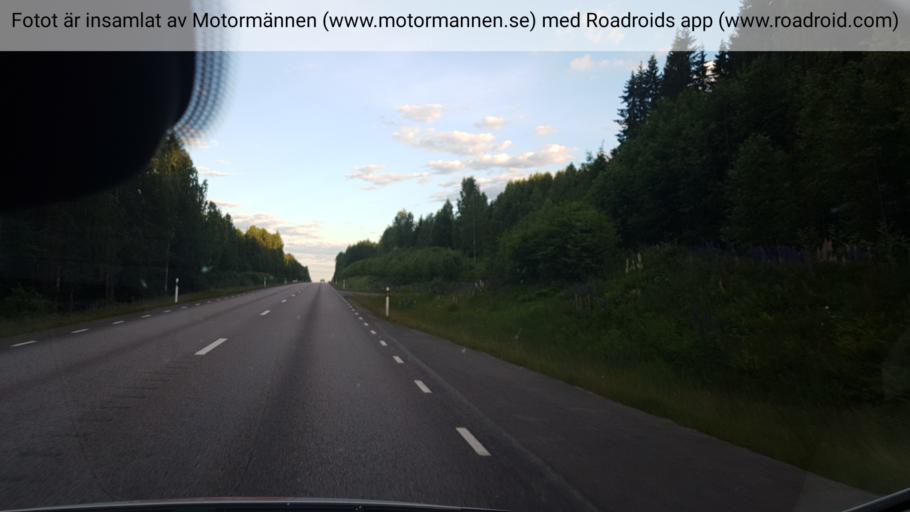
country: SE
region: Vaermland
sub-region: Torsby Kommun
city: Torsby
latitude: 59.9966
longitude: 13.0941
